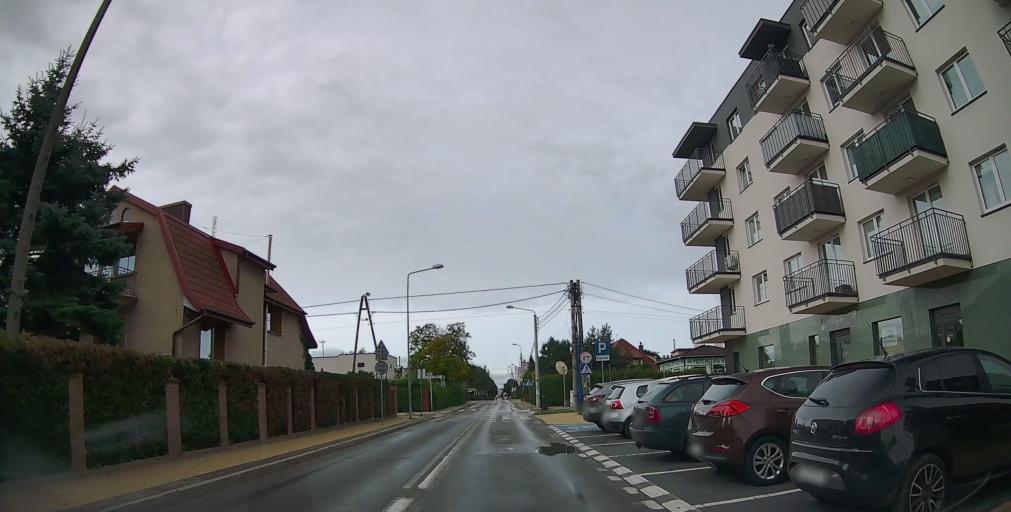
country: PL
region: Masovian Voivodeship
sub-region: Powiat grojecki
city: Grojec
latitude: 51.8682
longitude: 20.8789
